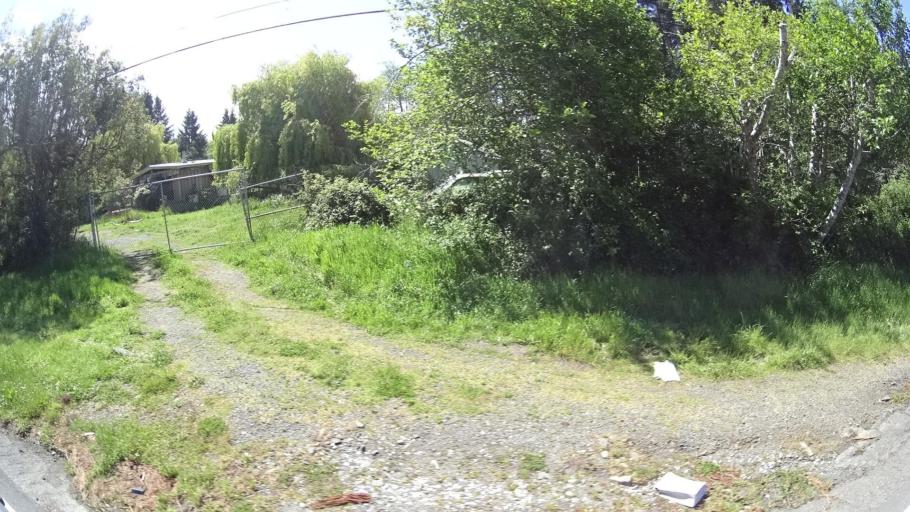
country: US
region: California
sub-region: Humboldt County
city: McKinleyville
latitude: 40.9567
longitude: -124.0918
